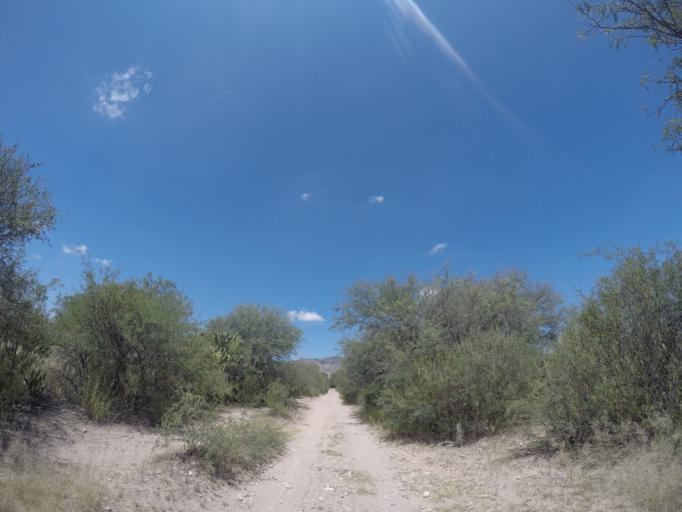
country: MX
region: San Luis Potosi
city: La Pila
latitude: 21.9822
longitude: -100.8961
